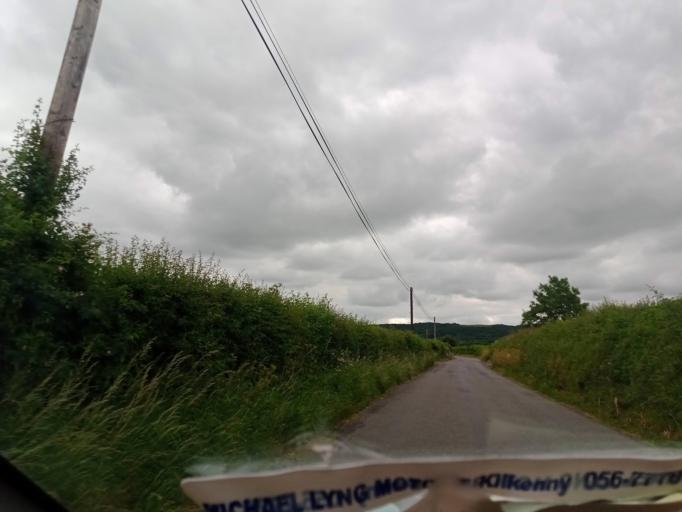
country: IE
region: Leinster
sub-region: Kilkenny
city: Ballyragget
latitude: 52.7384
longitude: -7.4158
